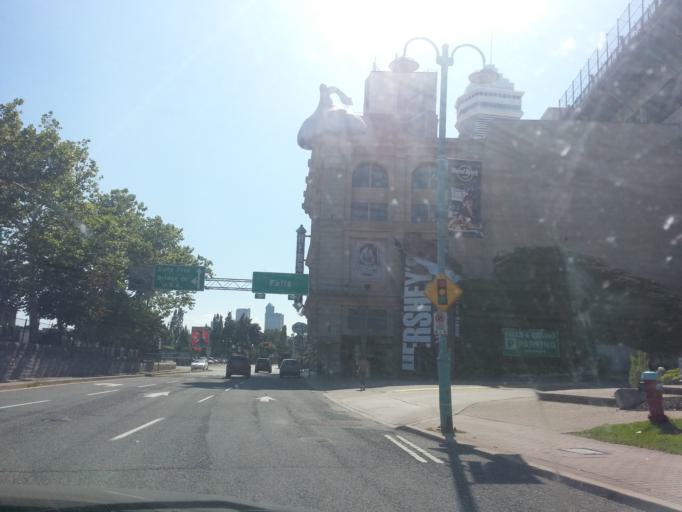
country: CA
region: Ontario
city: Niagara Falls
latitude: 43.0926
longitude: -79.0704
